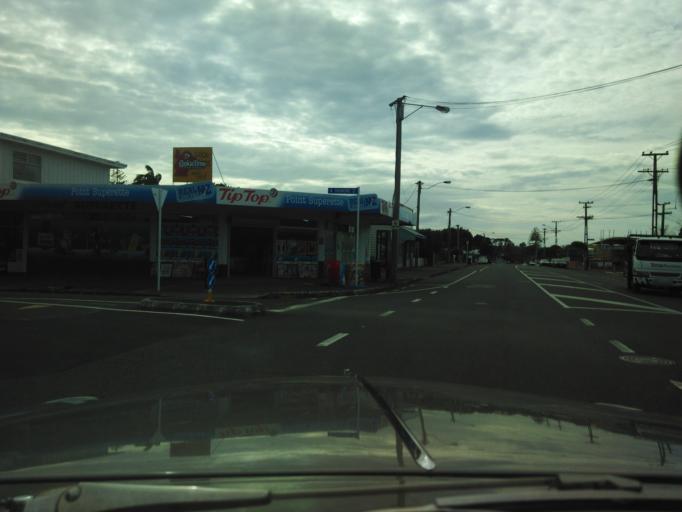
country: NZ
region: Auckland
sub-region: Auckland
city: Rosebank
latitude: -36.8596
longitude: 174.7024
